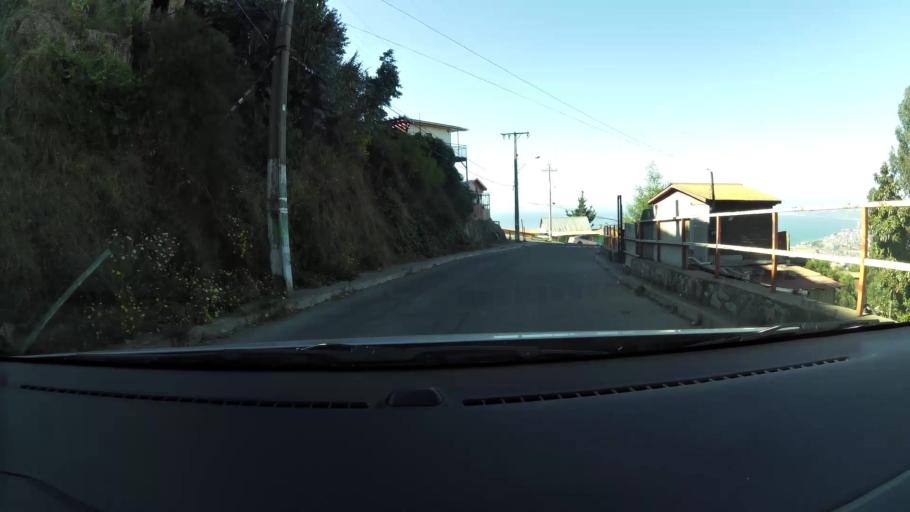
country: CL
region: Valparaiso
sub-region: Provincia de Valparaiso
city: Valparaiso
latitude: -33.0594
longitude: -71.6228
